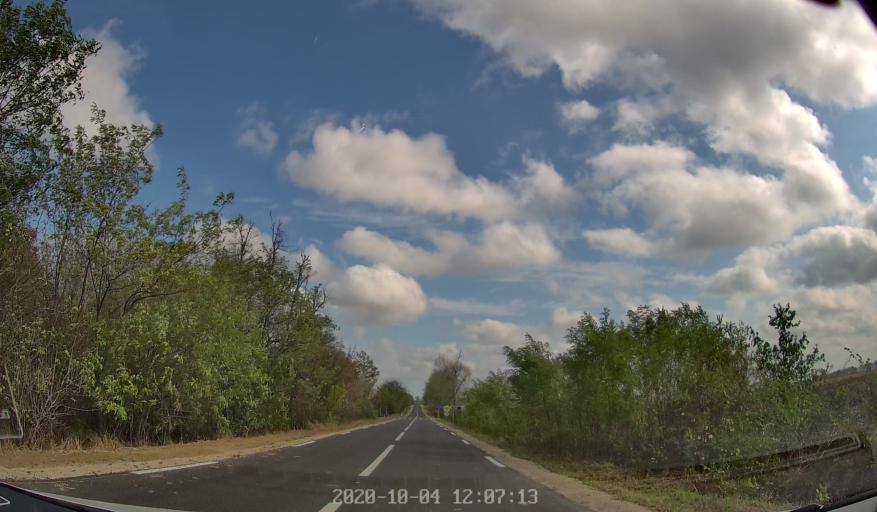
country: MD
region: Rezina
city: Saharna
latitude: 47.5855
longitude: 28.9701
